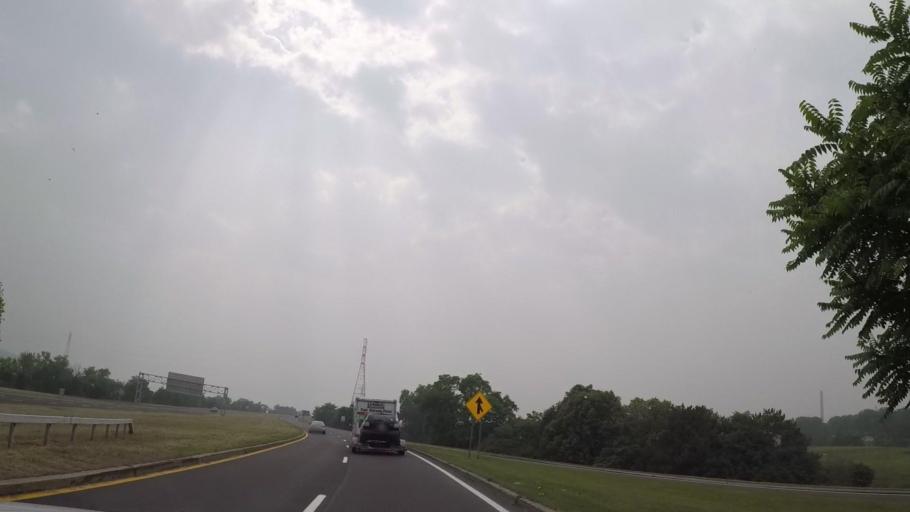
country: US
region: New York
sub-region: Niagara County
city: Niagara Falls
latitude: 43.0747
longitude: -78.9942
